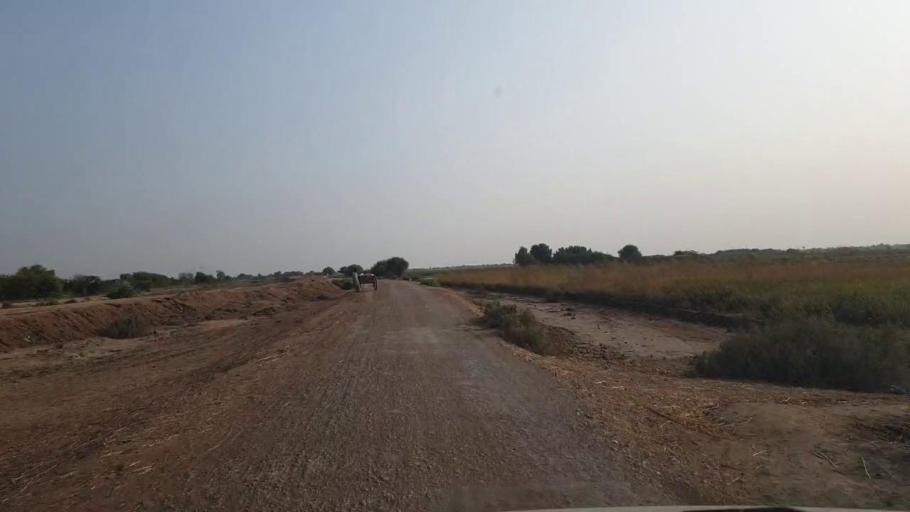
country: PK
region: Sindh
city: Matli
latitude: 25.0539
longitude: 68.7634
